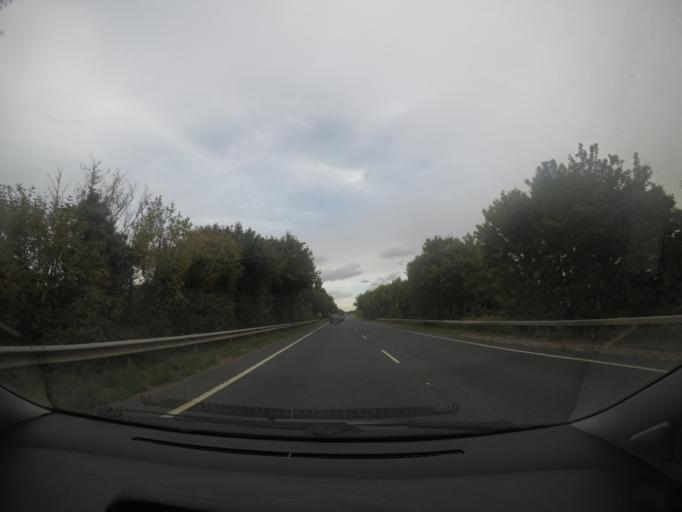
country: GB
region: England
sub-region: North Yorkshire
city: Riccall
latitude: 53.8351
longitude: -1.0546
